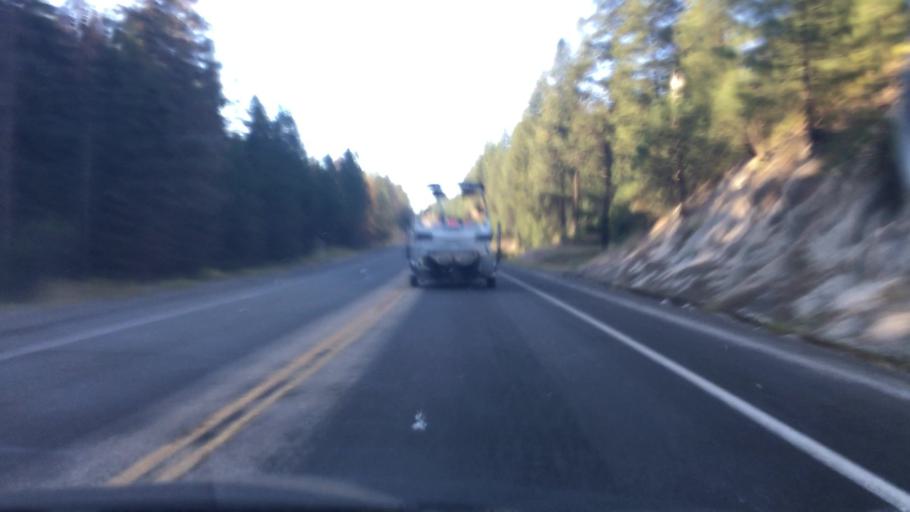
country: US
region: Idaho
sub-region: Valley County
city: Cascade
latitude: 44.5702
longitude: -116.0301
